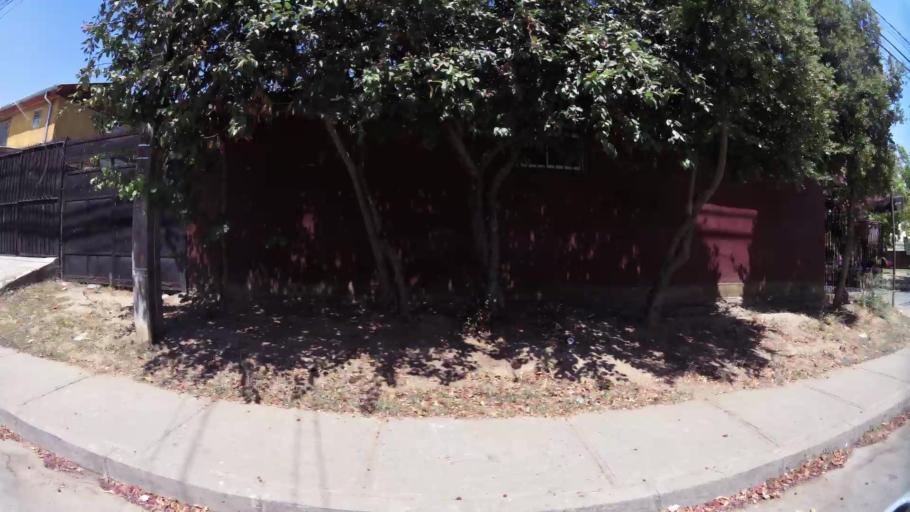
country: CL
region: Maule
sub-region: Provincia de Talca
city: Talca
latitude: -35.4325
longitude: -71.6316
